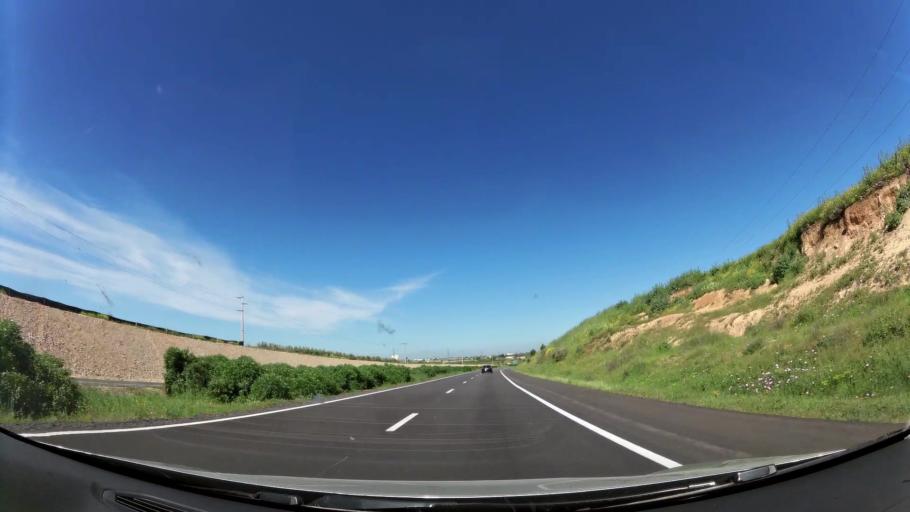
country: MA
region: Meknes-Tafilalet
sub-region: Meknes
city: Meknes
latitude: 33.8282
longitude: -5.5001
